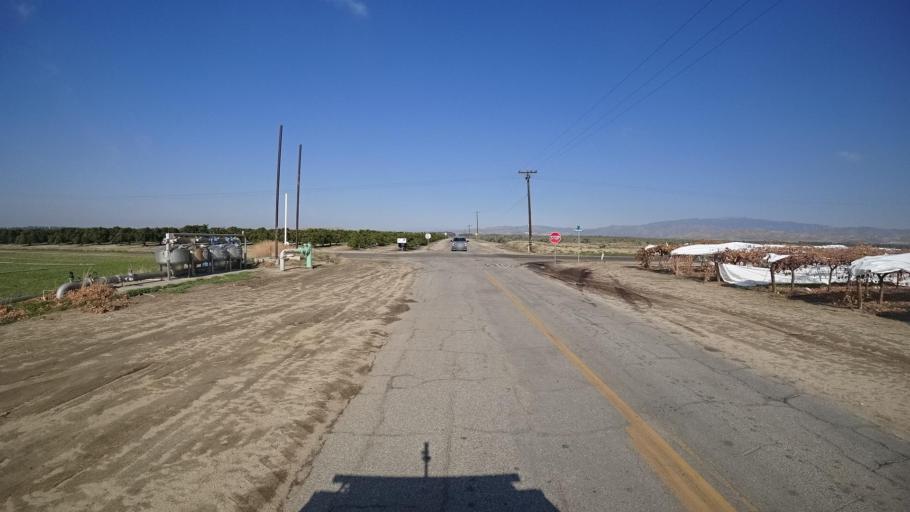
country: US
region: California
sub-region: Kern County
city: Arvin
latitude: 35.2671
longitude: -118.7889
